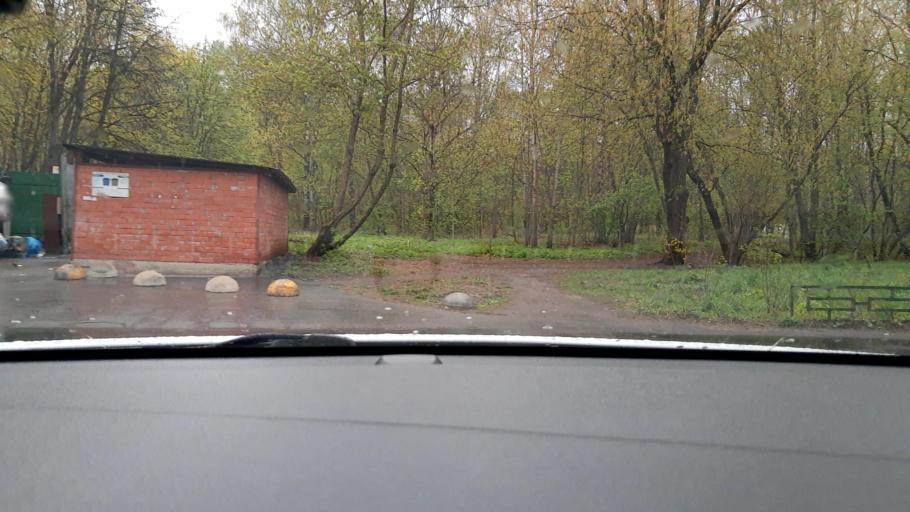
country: RU
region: Moscow
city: Rublevo
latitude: 55.7848
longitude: 37.3607
